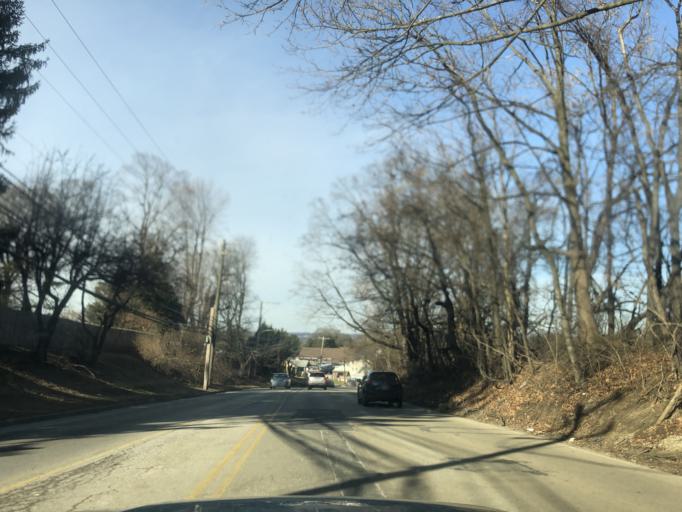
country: US
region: Pennsylvania
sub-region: Montgomery County
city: Plymouth Meeting
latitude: 40.0784
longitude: -75.2499
